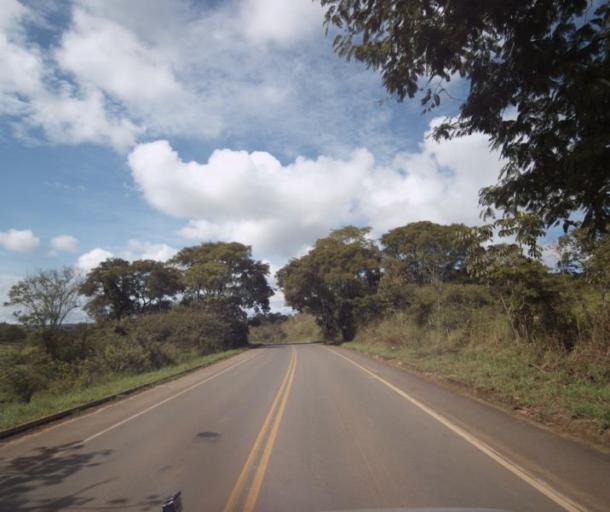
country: BR
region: Goias
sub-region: Pirenopolis
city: Pirenopolis
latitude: -15.9428
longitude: -48.8056
